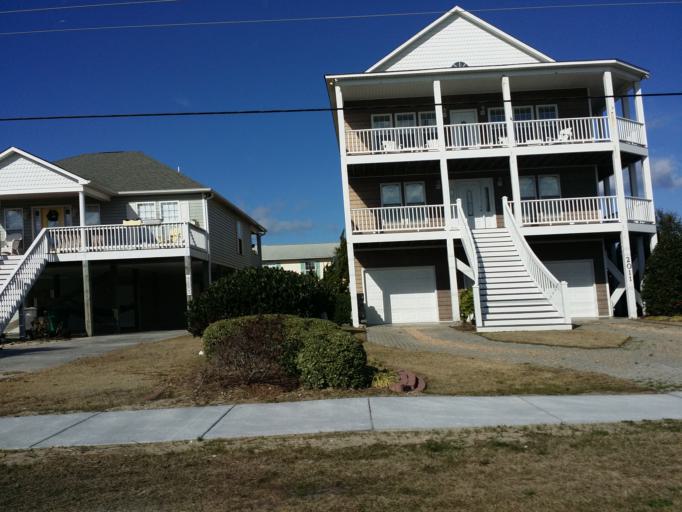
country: US
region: North Carolina
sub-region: Pender County
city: Surf City
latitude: 34.4457
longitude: -77.5130
